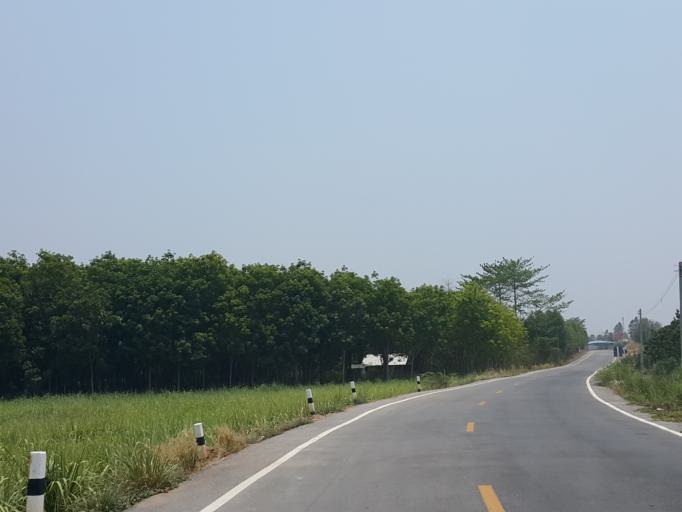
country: TH
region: Kamphaeng Phet
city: Khlong Lan
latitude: 16.0582
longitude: 99.3462
